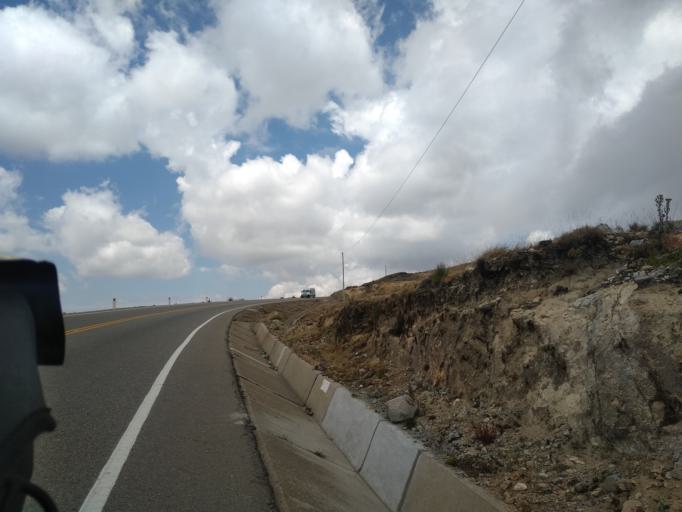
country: PE
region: La Libertad
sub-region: Provincia de Santiago de Chuco
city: Quiruvilca
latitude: -7.9519
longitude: -78.1914
